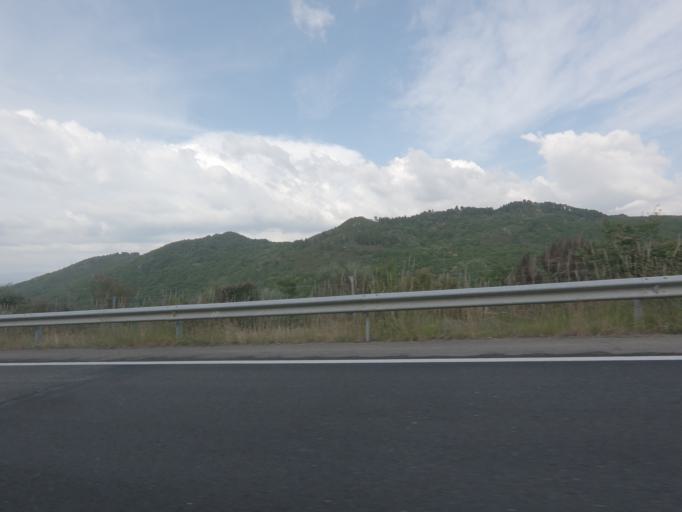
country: ES
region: Galicia
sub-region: Provincia de Ourense
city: Ambia
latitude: 42.1748
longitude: -7.7637
